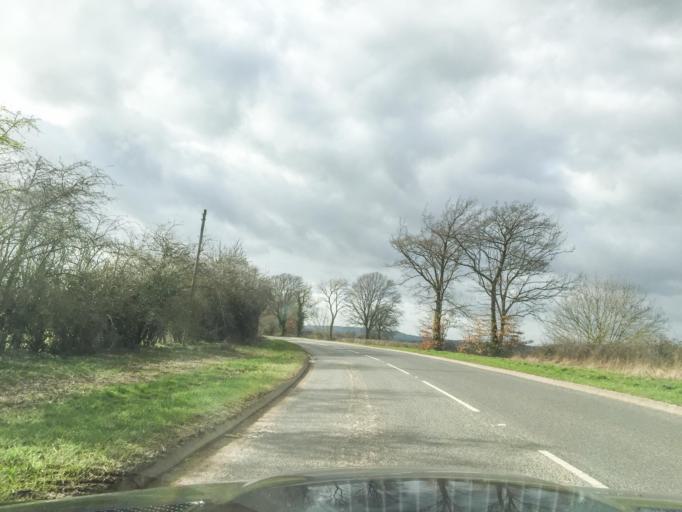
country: GB
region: England
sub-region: Warwickshire
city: Shipston on Stour
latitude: 52.0625
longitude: -1.5775
